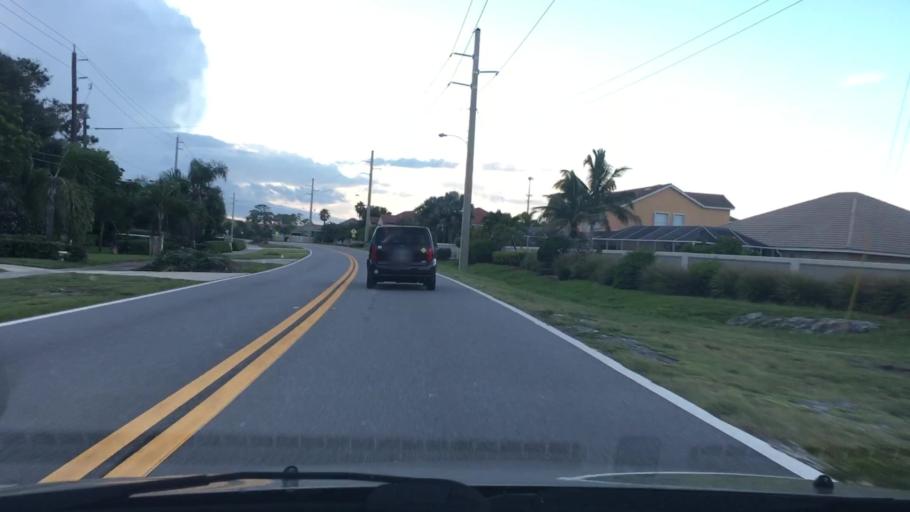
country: US
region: Florida
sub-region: Brevard County
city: Indian Harbour Beach
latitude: 28.1320
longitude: -80.5923
